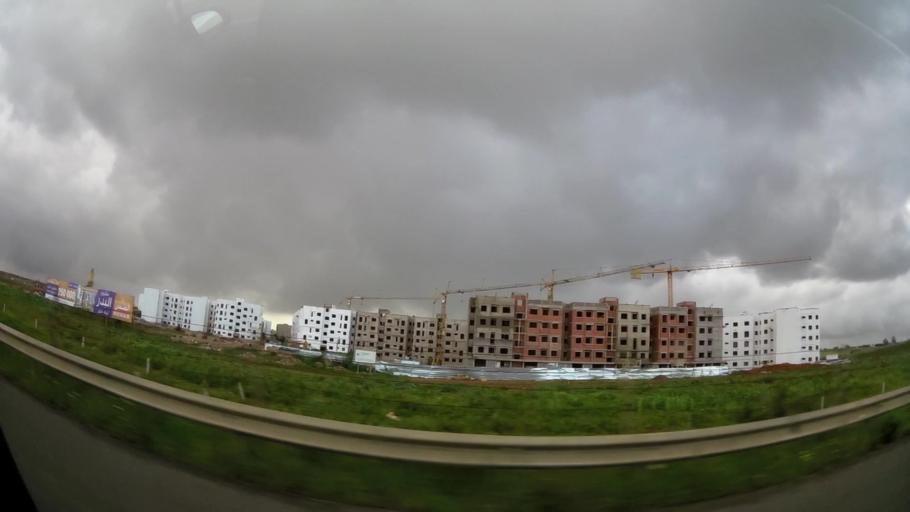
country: MA
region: Grand Casablanca
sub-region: Mediouna
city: Tit Mellil
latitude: 33.5685
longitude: -7.4647
